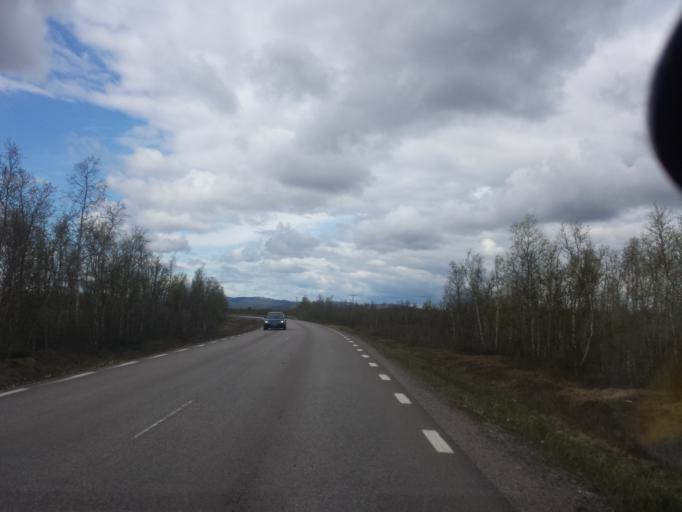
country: SE
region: Norrbotten
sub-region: Kiruna Kommun
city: Kiruna
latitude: 67.8929
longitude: 20.1305
